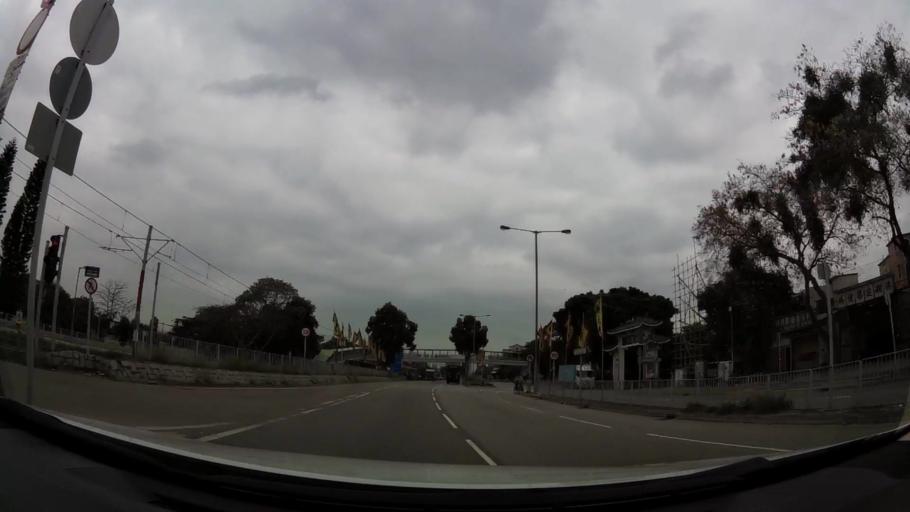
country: HK
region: Tuen Mun
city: Tuen Mun
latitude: 22.4291
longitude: 113.9916
